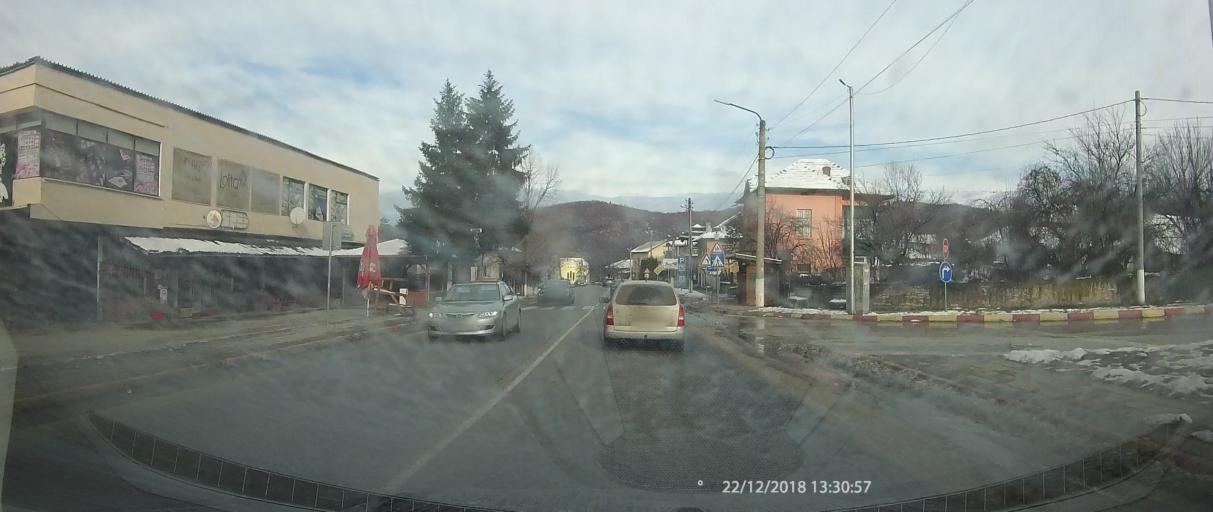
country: BG
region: Lovech
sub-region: Obshtina Yablanitsa
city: Yablanitsa
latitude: 43.0920
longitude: 24.1505
